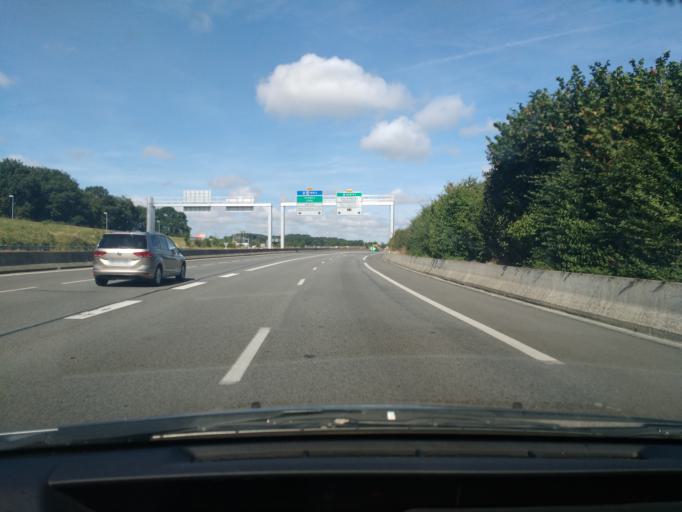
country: FR
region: Pays de la Loire
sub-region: Departement de Maine-et-Loire
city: Beaucouze
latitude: 47.4694
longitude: -0.6107
